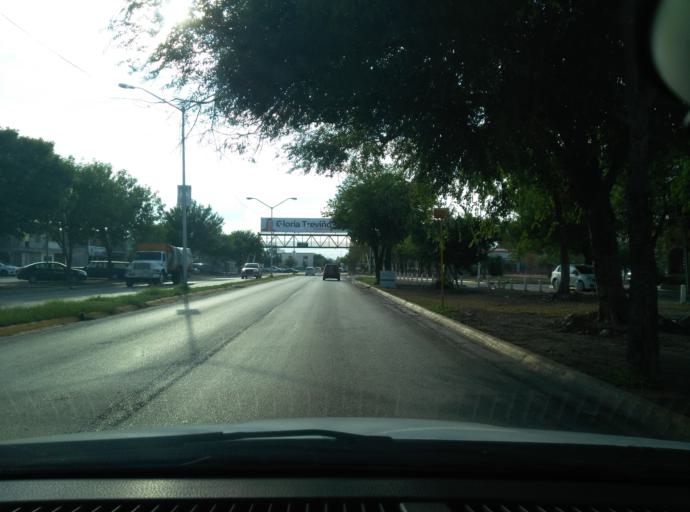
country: MX
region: Nuevo Leon
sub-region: Apodaca
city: Fraccionamiento Cosmopolis Octavo Sector
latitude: 25.7684
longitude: -100.2466
